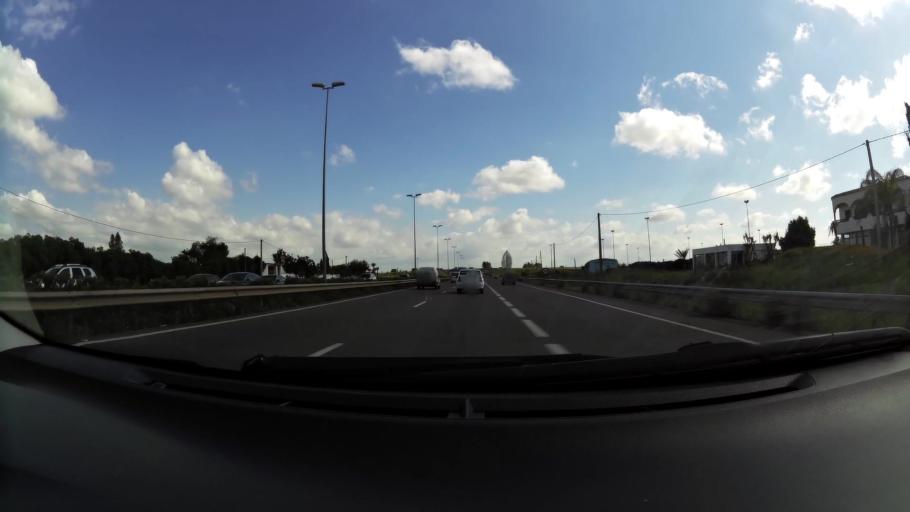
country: MA
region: Chaouia-Ouardigha
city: Nouaseur
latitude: 33.3944
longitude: -7.6206
